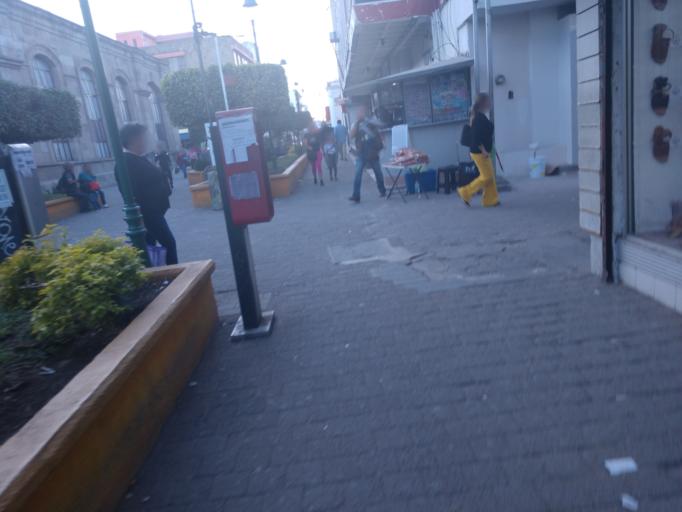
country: MX
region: Nayarit
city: Tepic
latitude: 21.5128
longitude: -104.8925
